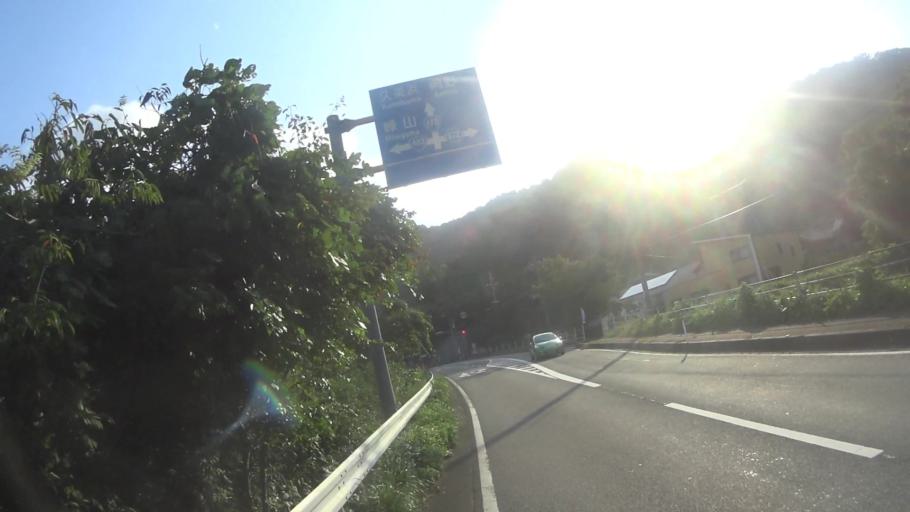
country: JP
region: Kyoto
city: Miyazu
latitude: 35.7292
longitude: 135.1018
